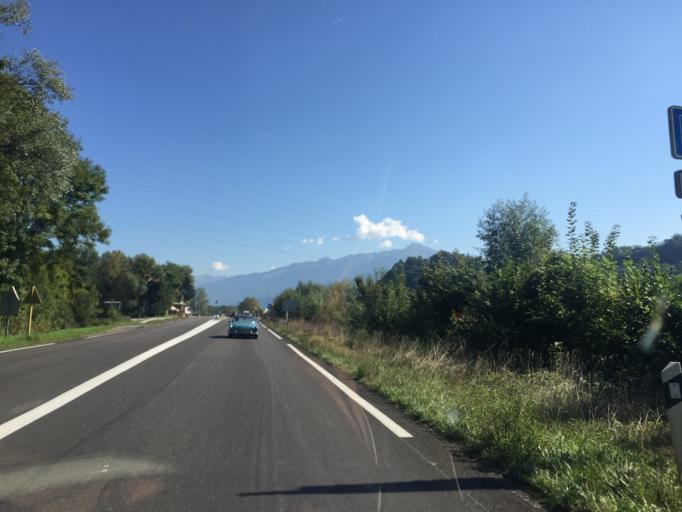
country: FR
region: Rhone-Alpes
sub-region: Departement de la Savoie
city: Coise-Saint-Jean-Pied-Gauthier
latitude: 45.5509
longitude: 6.1569
